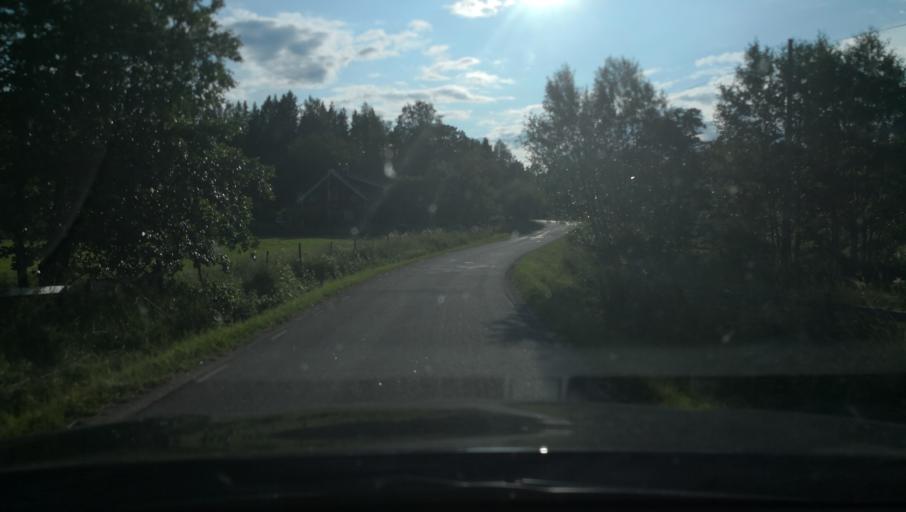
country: SE
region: Uppsala
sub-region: Osthammars Kommun
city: Osterbybruk
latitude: 60.0172
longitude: 17.9337
